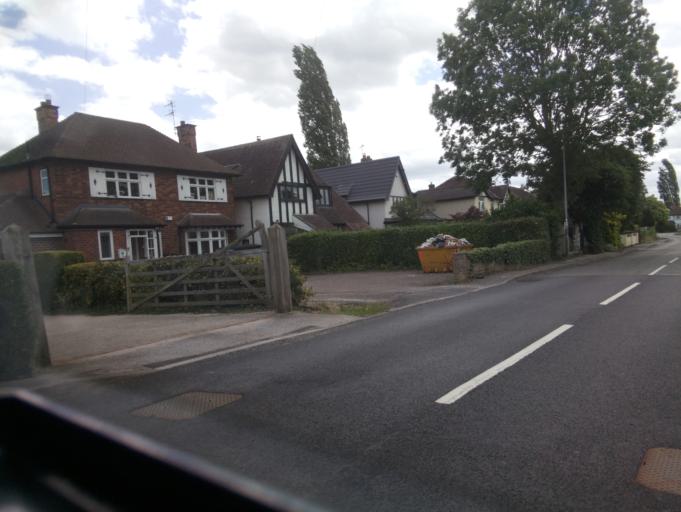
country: GB
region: England
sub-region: Nottinghamshire
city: West Bridgford
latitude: 52.8997
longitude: -1.0943
